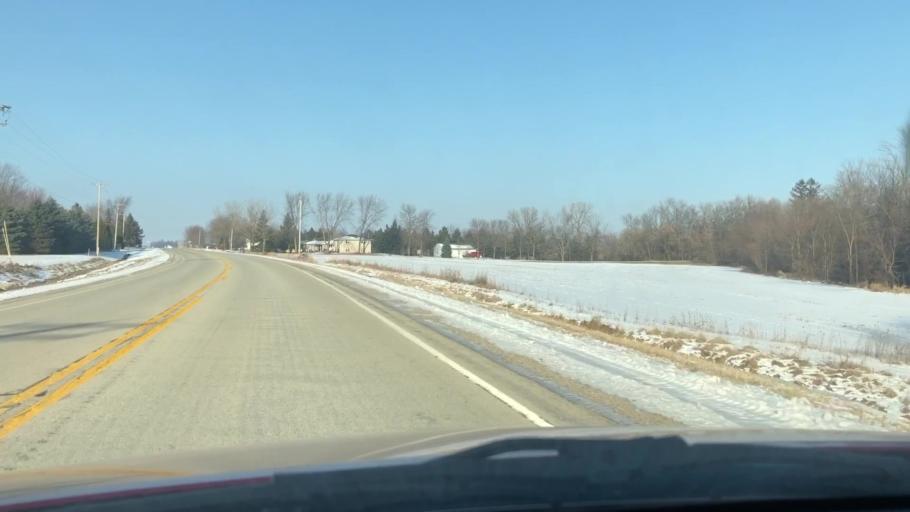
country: US
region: Wisconsin
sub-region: Outagamie County
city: Black Creek
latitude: 44.3968
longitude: -88.3746
